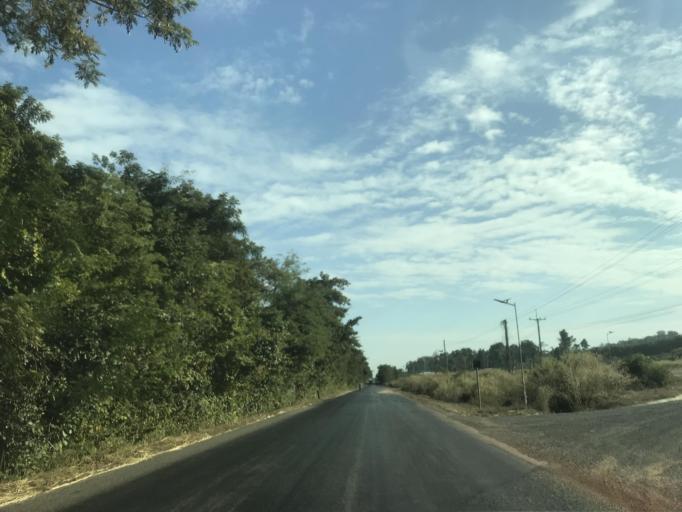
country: LA
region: Khammouan
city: Muang Hinboun
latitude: 17.7858
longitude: 104.4960
